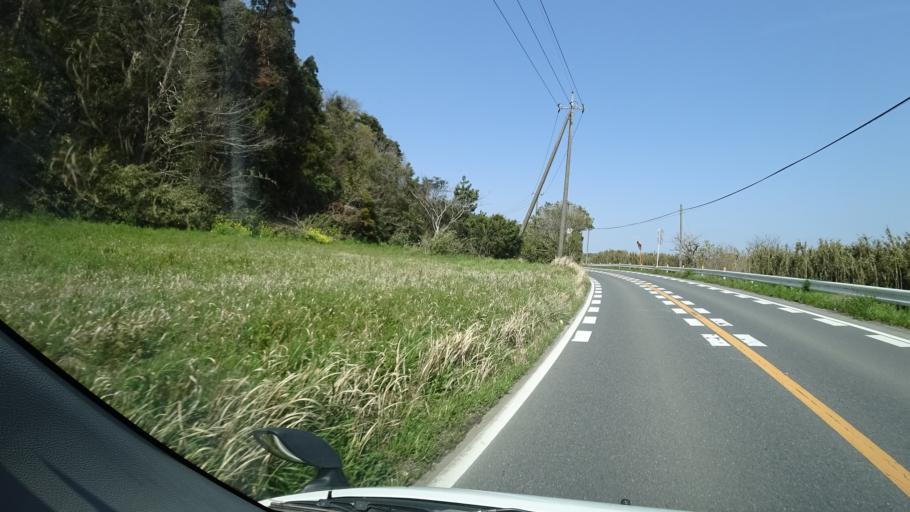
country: JP
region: Chiba
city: Yokaichiba
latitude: 35.6957
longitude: 140.4611
